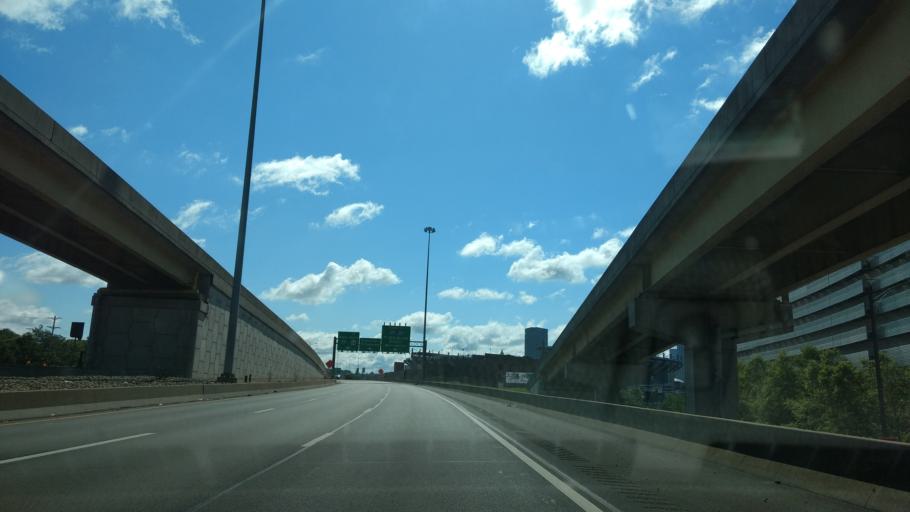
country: US
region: Pennsylvania
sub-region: Allegheny County
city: Pittsburgh
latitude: 40.4492
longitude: -80.0237
